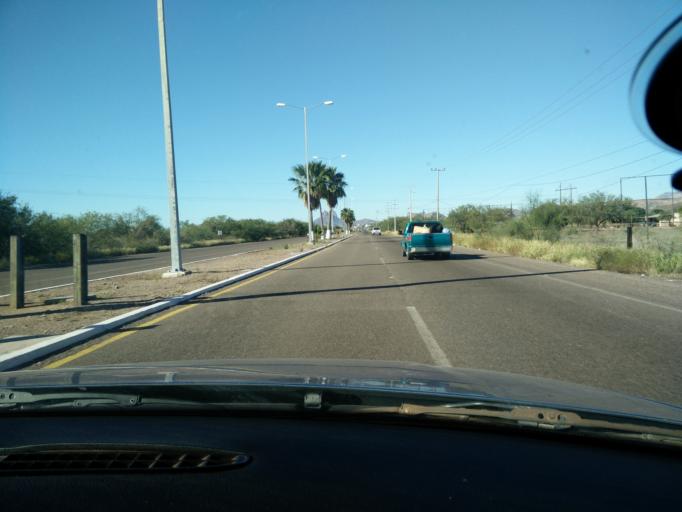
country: MX
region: Sonora
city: Heroica Guaymas
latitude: 27.9814
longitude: -110.9624
